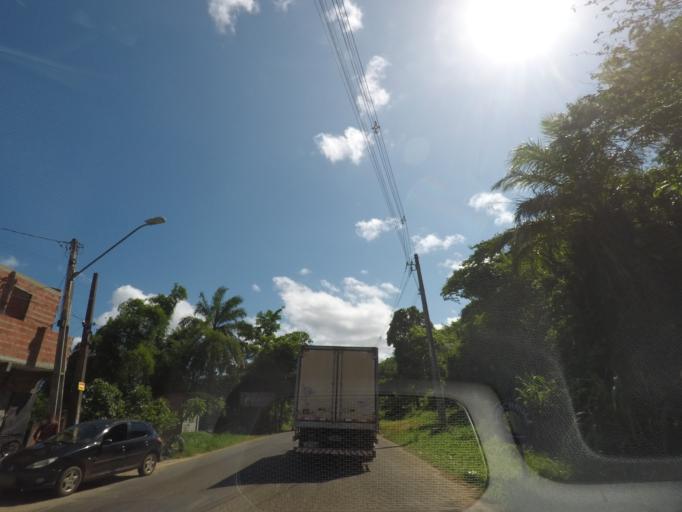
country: BR
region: Bahia
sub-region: Itubera
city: Itubera
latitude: -13.7510
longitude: -39.1533
